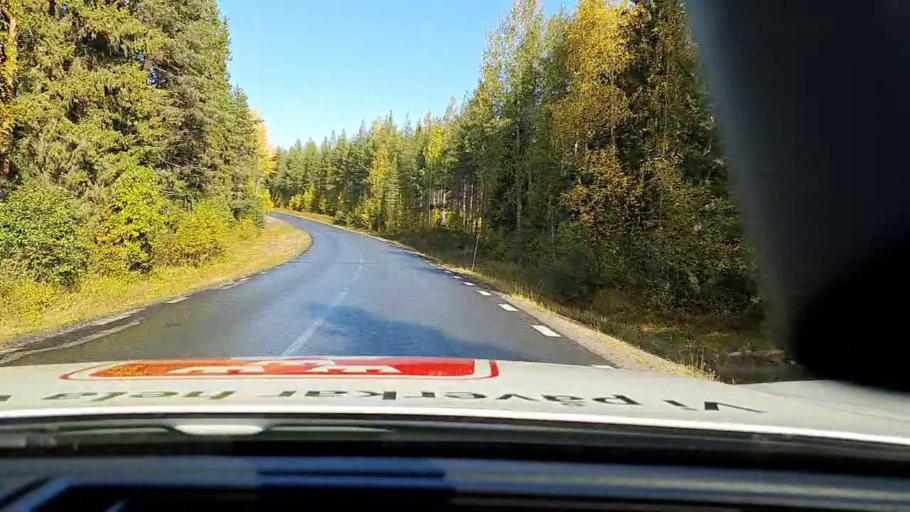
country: SE
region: Vaesterbotten
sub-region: Skelleftea Kommun
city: Langsele
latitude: 64.9619
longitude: 20.0436
